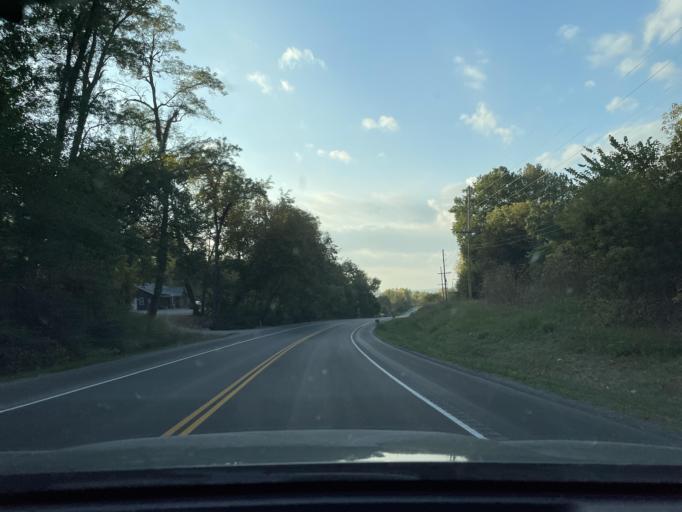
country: US
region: Missouri
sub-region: Andrew County
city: Country Club Village
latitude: 39.8563
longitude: -94.8745
